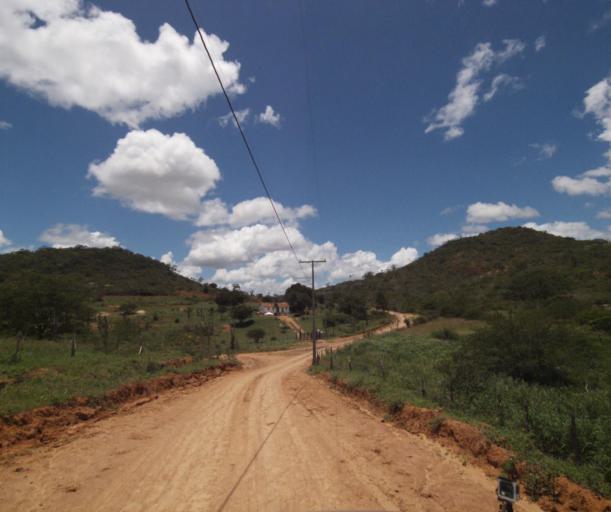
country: BR
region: Bahia
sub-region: Pocoes
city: Pocoes
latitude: -14.3802
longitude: -40.4105
